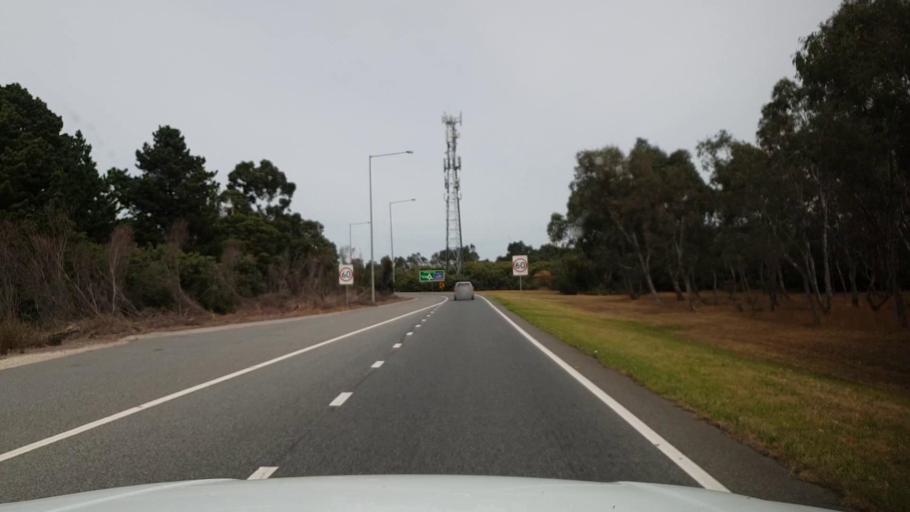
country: AU
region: Victoria
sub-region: Frankston
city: Seaford
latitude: -38.0963
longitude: 145.1484
